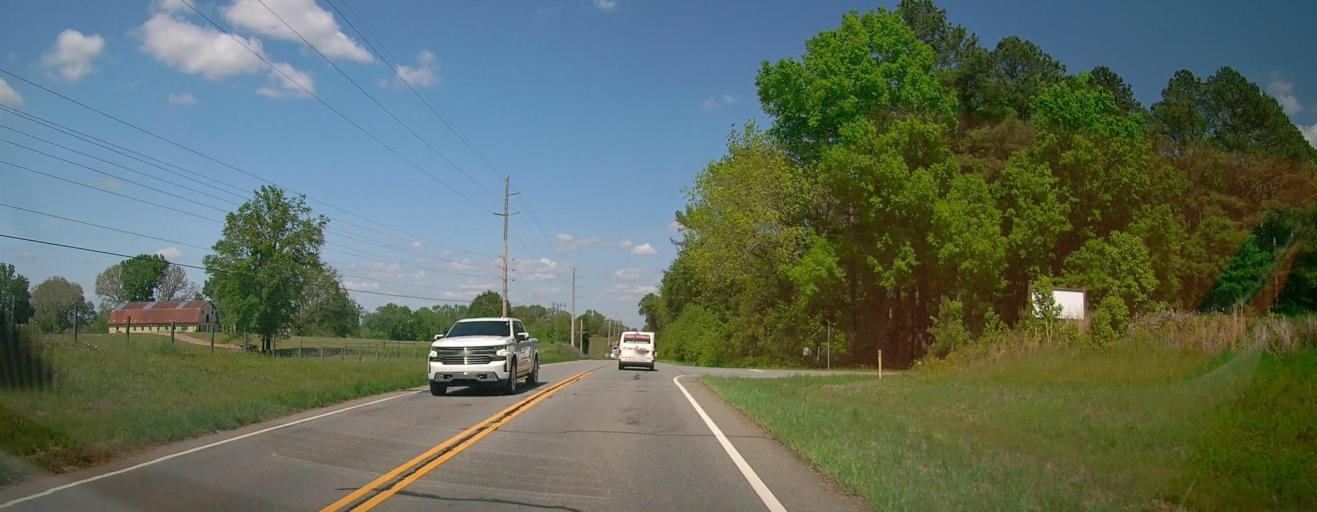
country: US
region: Georgia
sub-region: Putnam County
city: Eatonton
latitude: 33.3632
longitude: -83.3386
